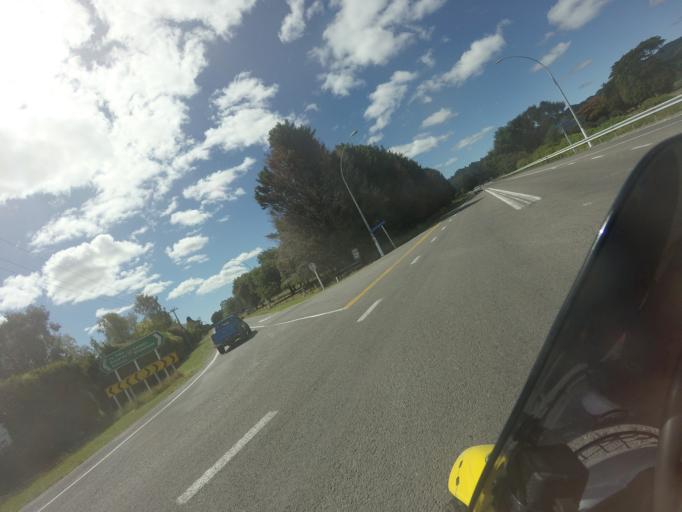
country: NZ
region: Bay of Plenty
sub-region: Whakatane District
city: Edgecumbe
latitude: -38.0233
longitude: 176.8382
